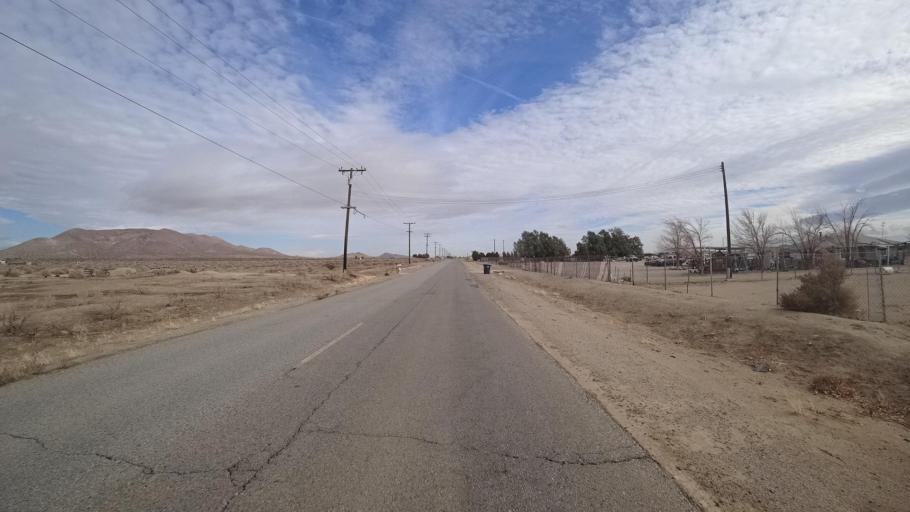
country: US
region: California
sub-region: Kern County
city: Rosamond
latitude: 34.8636
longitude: -118.3022
